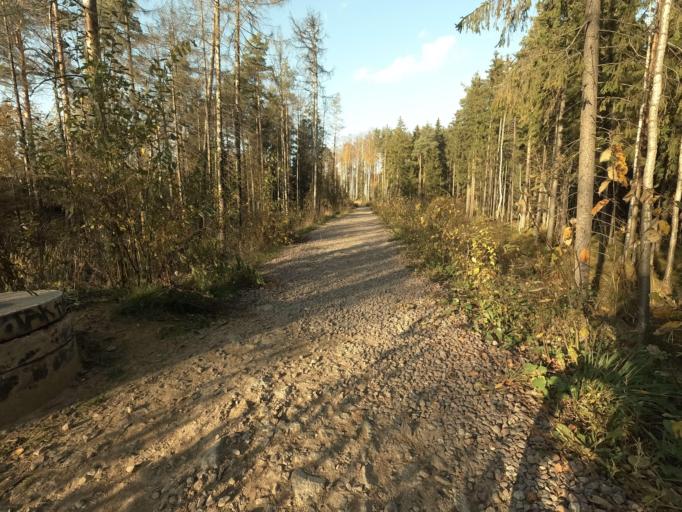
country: RU
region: Leningrad
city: Sertolovo
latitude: 60.1491
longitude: 30.2224
